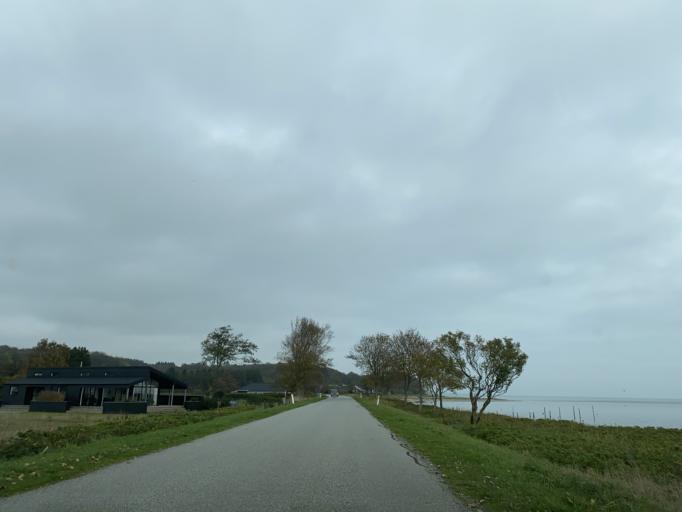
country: DK
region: South Denmark
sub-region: Aabenraa Kommune
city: Lojt Kirkeby
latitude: 55.1585
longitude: 9.5018
